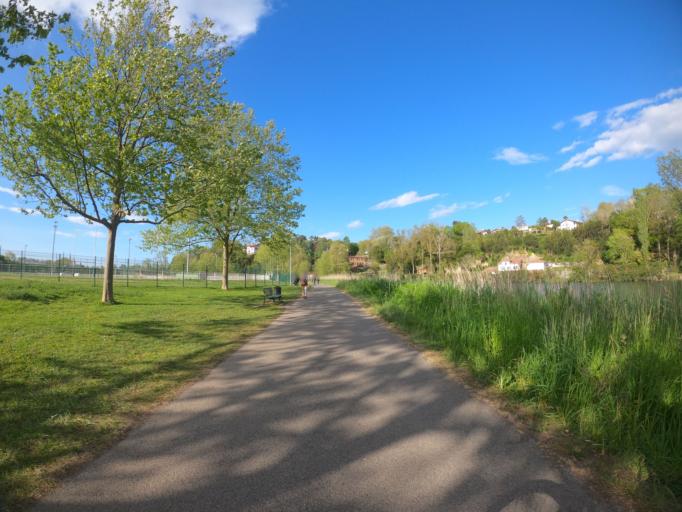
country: FR
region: Aquitaine
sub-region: Departement des Pyrenees-Atlantiques
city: Bayonne
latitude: 43.4800
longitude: -1.4711
